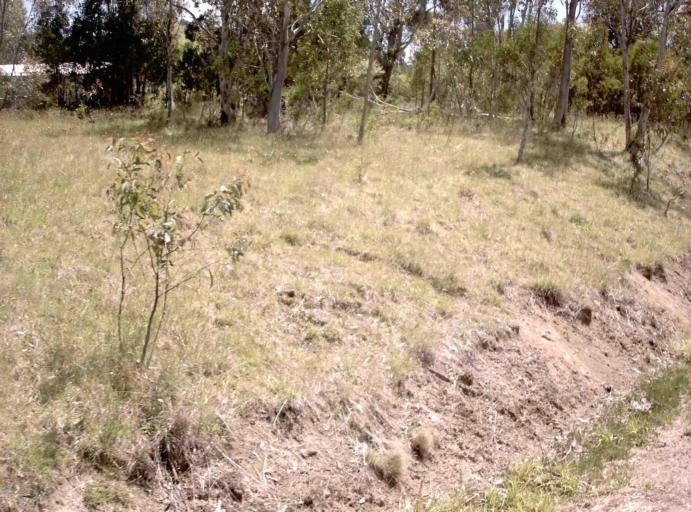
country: AU
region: New South Wales
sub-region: Snowy River
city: Jindabyne
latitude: -37.1124
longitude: 148.2493
